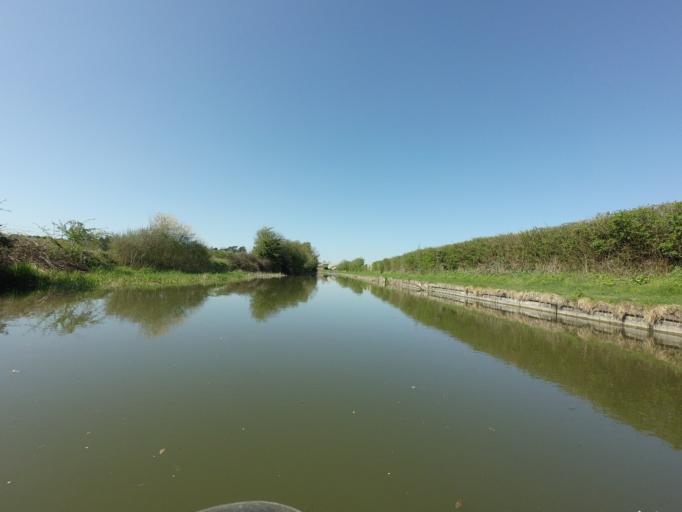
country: GB
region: England
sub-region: Hertfordshire
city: Tring
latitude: 51.7878
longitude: -0.6163
